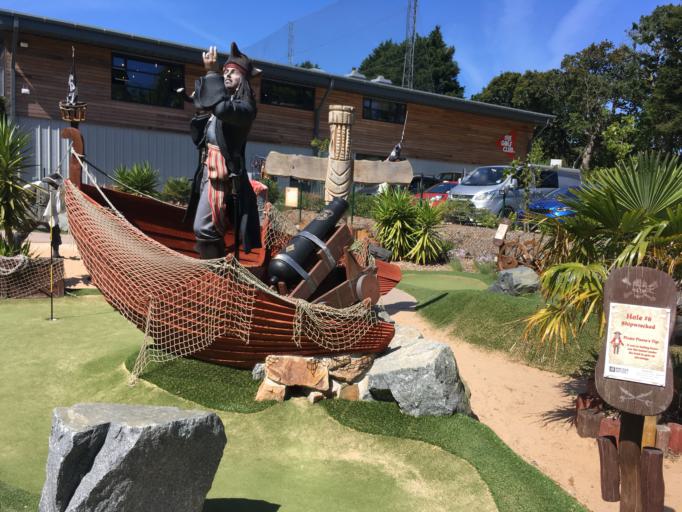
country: GG
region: St Peter Port
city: Saint Peter Port
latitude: 49.4595
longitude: -2.5643
